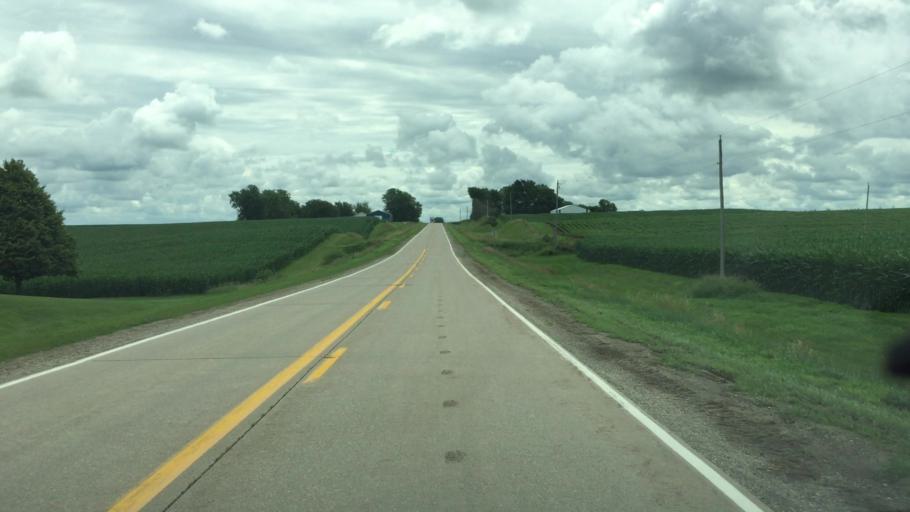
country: US
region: Iowa
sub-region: Jasper County
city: Monroe
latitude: 41.5807
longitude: -93.1176
